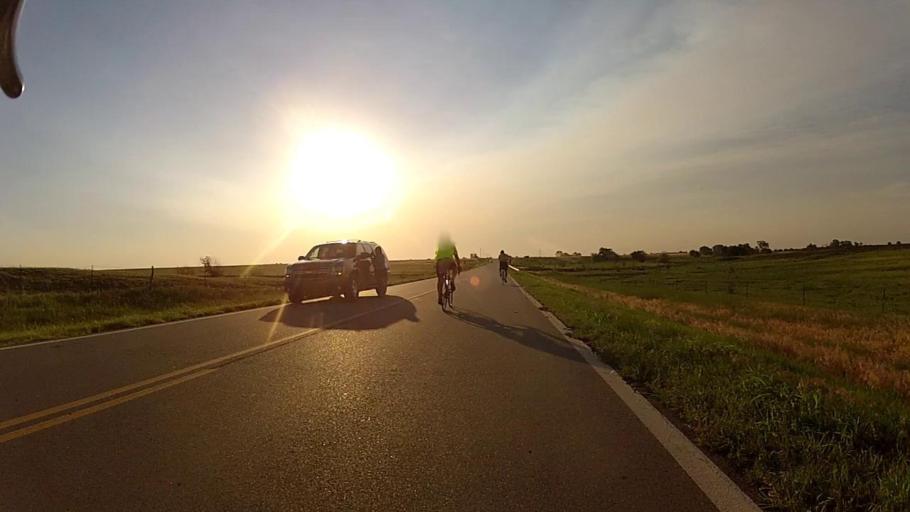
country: US
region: Kansas
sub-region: Harper County
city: Anthony
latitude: 37.1533
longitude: -97.8981
